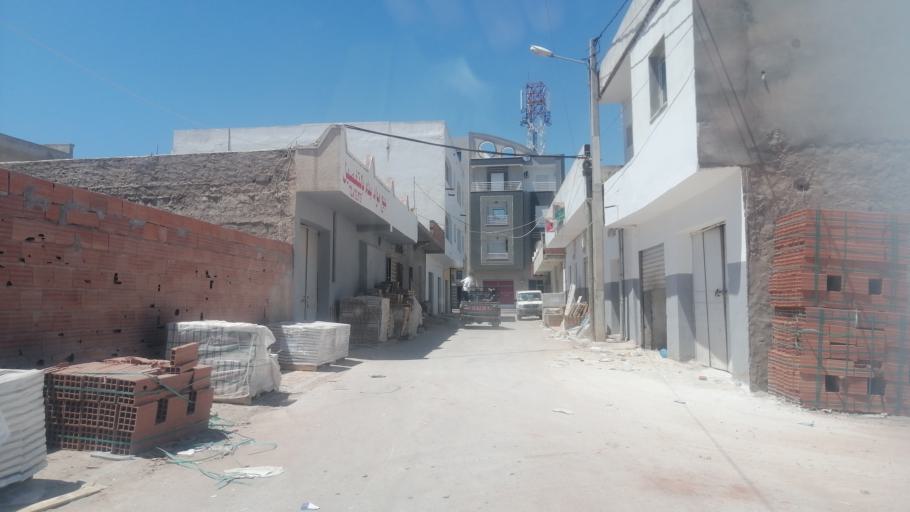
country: TN
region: Al Qayrawan
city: Sbikha
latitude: 36.1172
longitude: 10.0967
